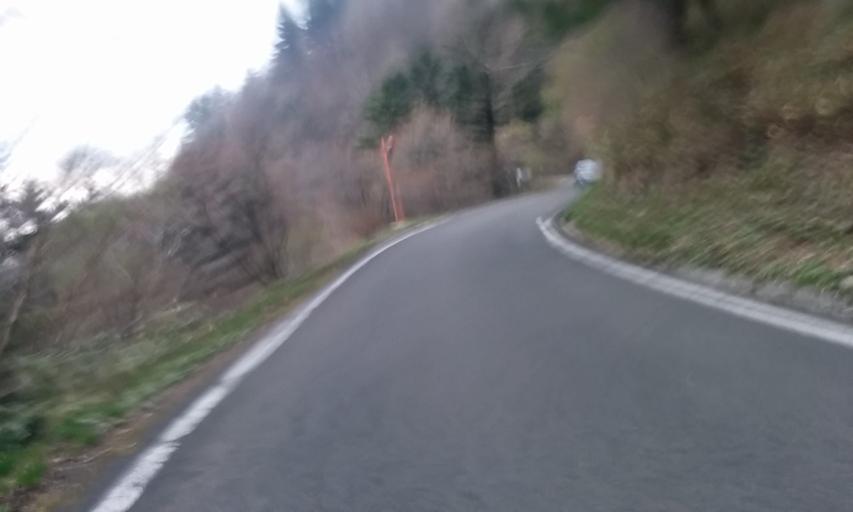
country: JP
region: Ehime
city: Saijo
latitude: 33.7832
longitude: 133.2405
